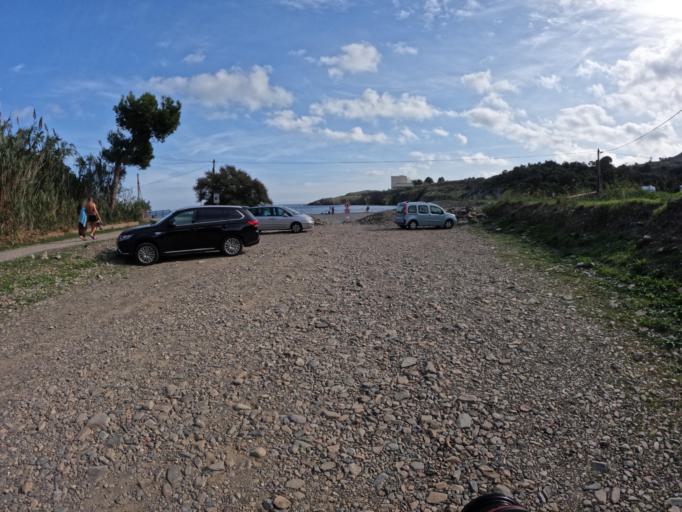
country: FR
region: Languedoc-Roussillon
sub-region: Departement des Pyrenees-Orientales
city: Cervera de la Marenda
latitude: 42.4605
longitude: 3.1561
